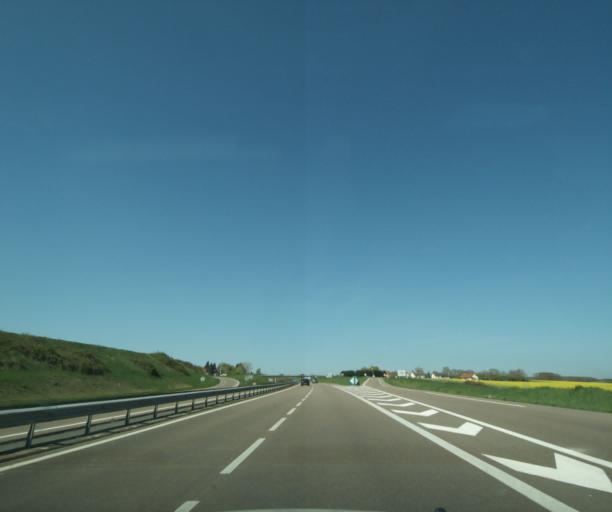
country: FR
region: Bourgogne
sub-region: Departement de la Nievre
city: Cosne-Cours-sur-Loire
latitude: 47.4130
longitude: 2.9464
